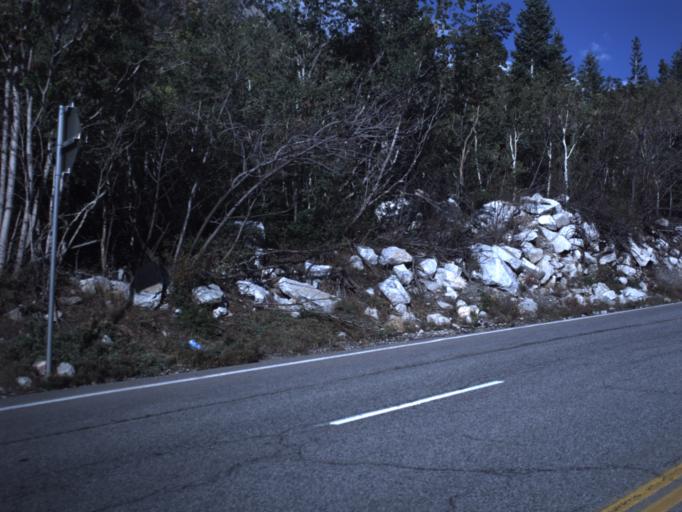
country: US
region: Utah
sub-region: Salt Lake County
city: Granite
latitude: 40.5711
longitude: -111.7068
